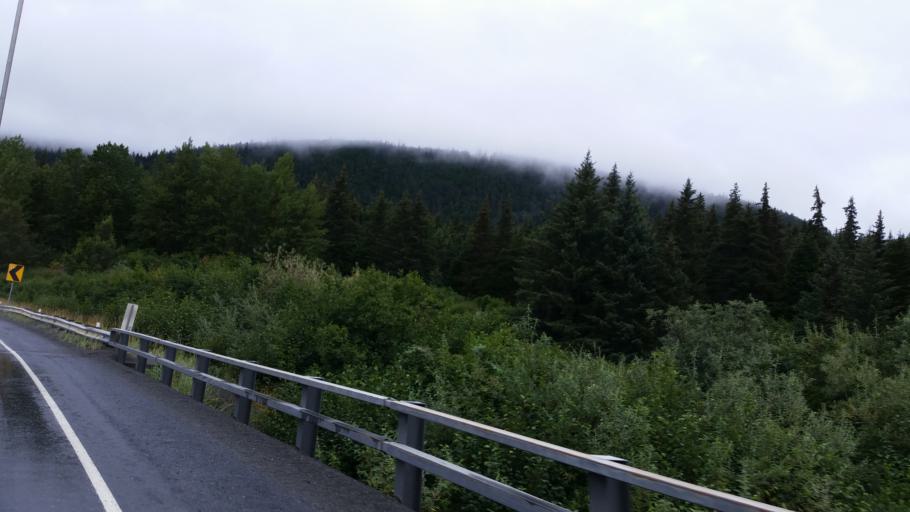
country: US
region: Alaska
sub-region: Anchorage Municipality
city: Girdwood
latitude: 60.8468
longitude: -149.0584
